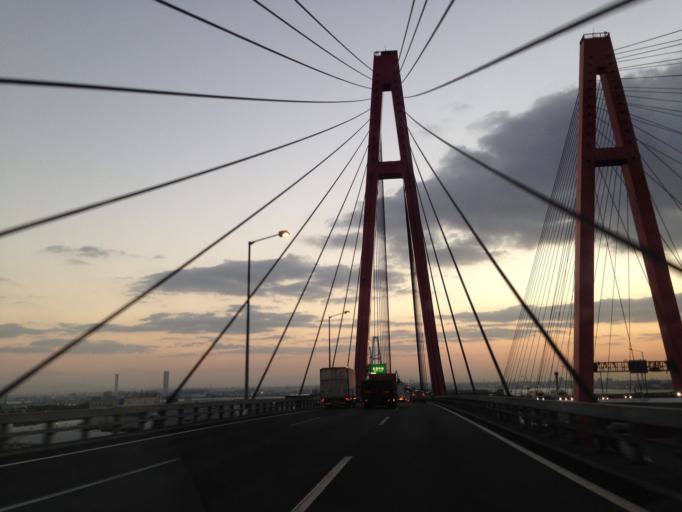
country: JP
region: Aichi
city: Kanie
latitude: 35.0520
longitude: 136.8348
